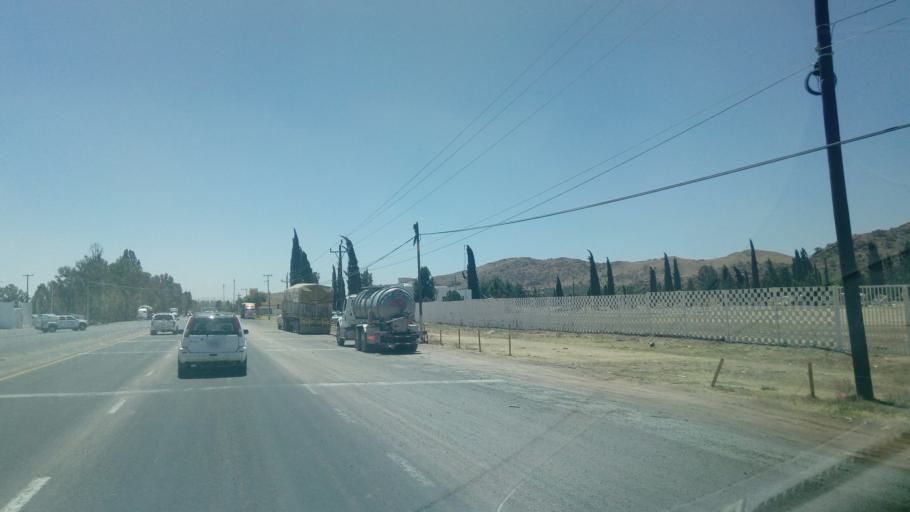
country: MX
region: Durango
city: Victoria de Durango
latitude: 24.0786
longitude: -104.6671
